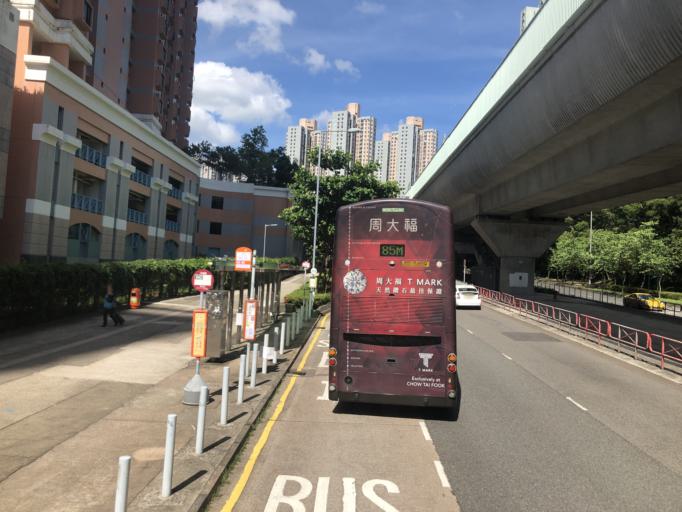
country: HK
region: Sai Kung
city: Sai Kung
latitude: 22.4259
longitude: 114.2362
